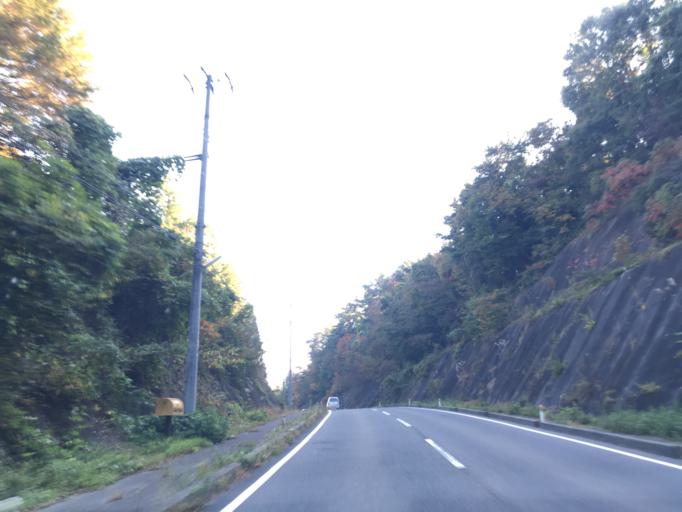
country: JP
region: Fukushima
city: Koriyama
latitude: 37.4124
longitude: 140.2700
